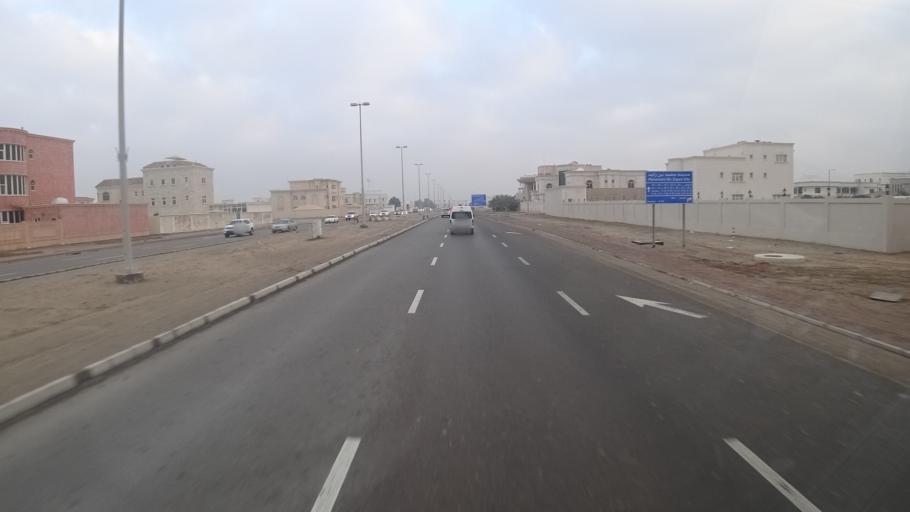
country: AE
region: Abu Dhabi
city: Abu Dhabi
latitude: 24.3217
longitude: 54.5746
